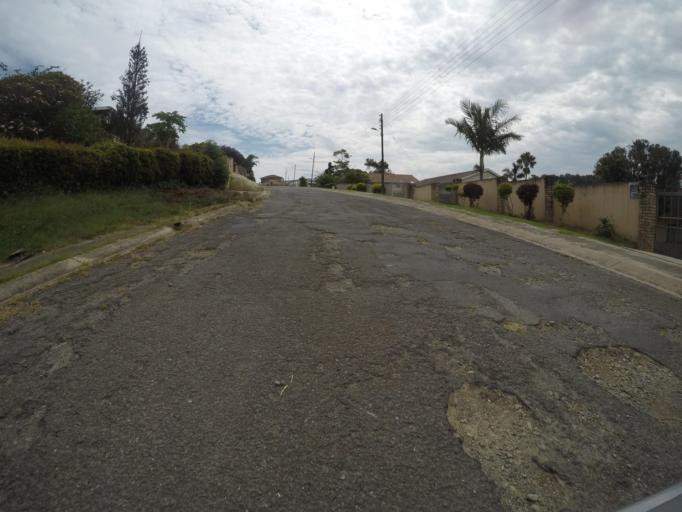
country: ZA
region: Eastern Cape
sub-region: Buffalo City Metropolitan Municipality
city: East London
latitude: -32.9942
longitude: 27.8723
